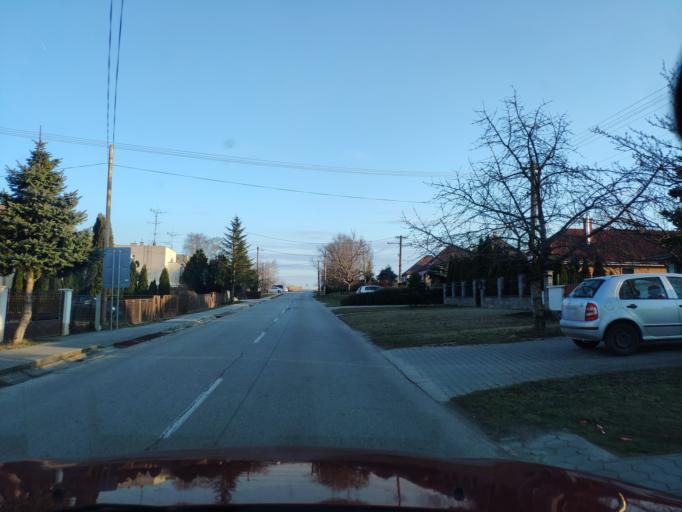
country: SK
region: Nitriansky
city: Sellye
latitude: 48.2719
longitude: 17.8347
